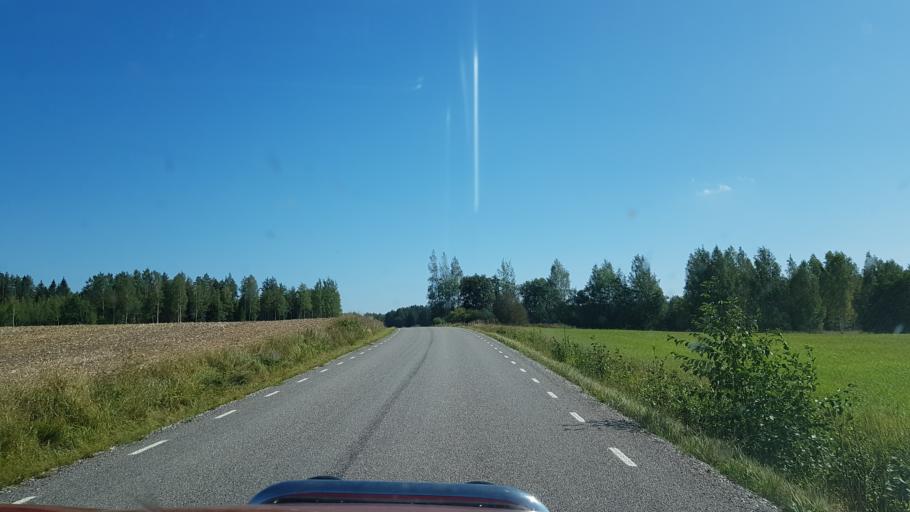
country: EE
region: Polvamaa
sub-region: Polva linn
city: Polva
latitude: 58.2092
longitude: 27.1173
